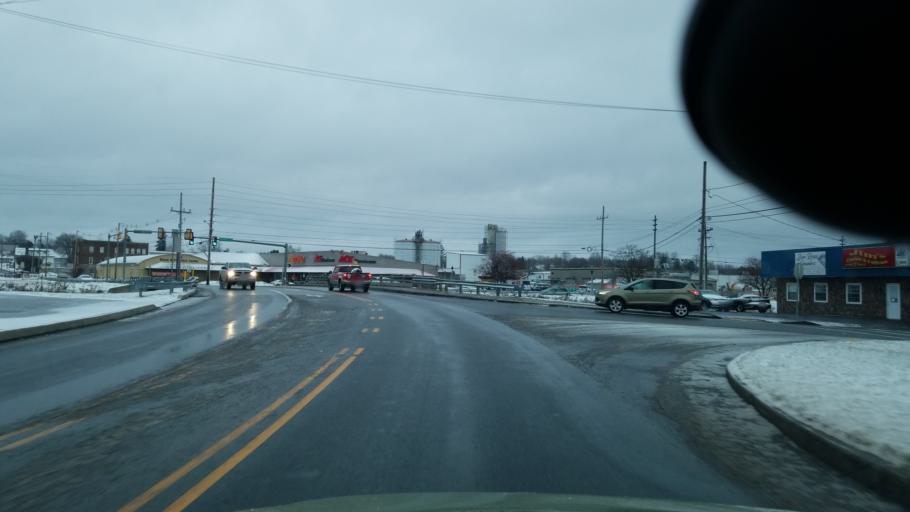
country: US
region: Pennsylvania
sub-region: Clearfield County
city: DuBois
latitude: 41.1253
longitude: -78.7642
